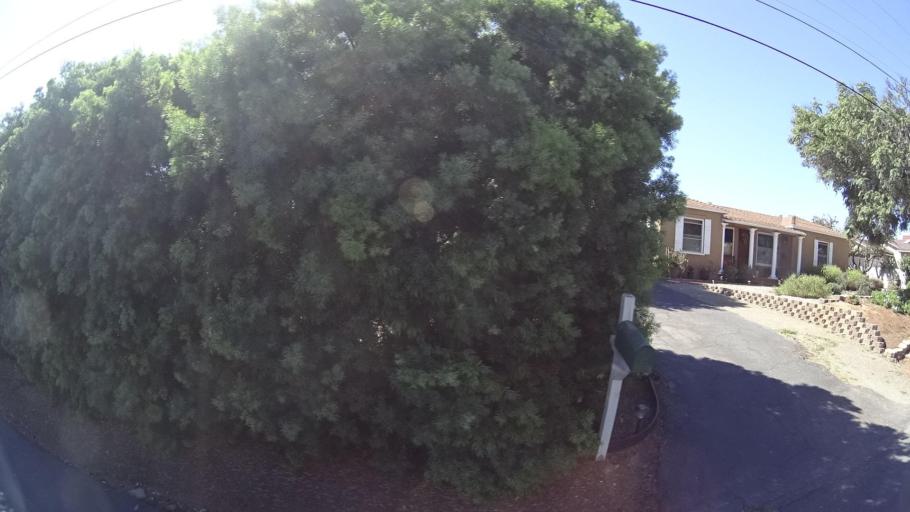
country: US
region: California
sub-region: San Diego County
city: Bonita
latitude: 32.6538
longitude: -117.0553
